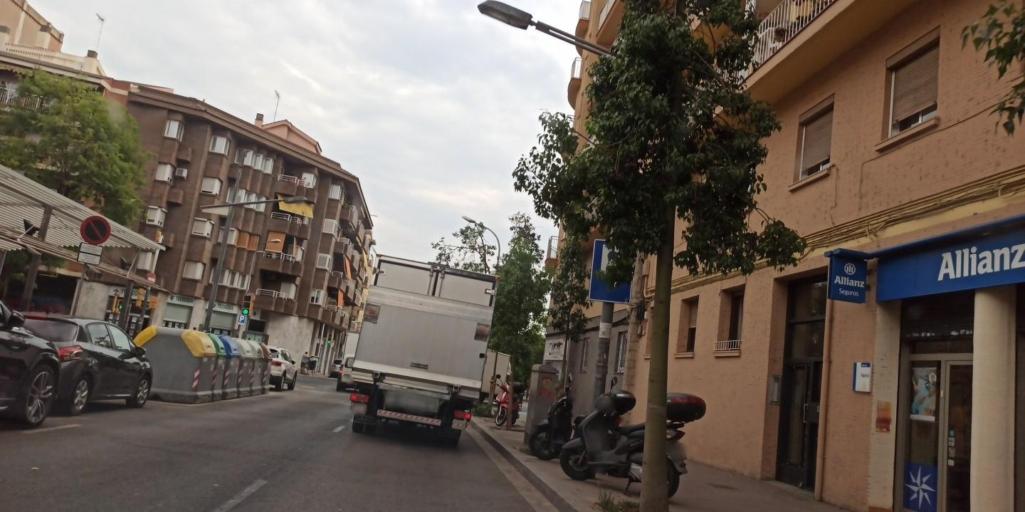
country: ES
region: Catalonia
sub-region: Provincia de Barcelona
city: Horta-Guinardo
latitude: 41.4278
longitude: 2.1744
